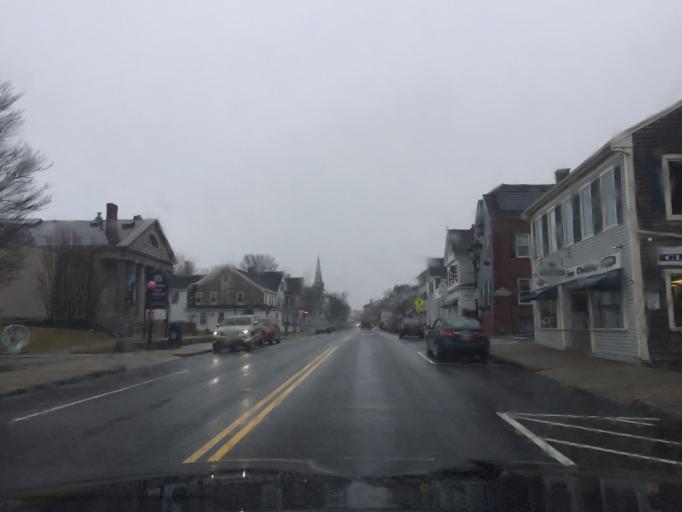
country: US
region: Massachusetts
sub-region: Plymouth County
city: Plymouth
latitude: 41.9592
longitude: -70.6687
